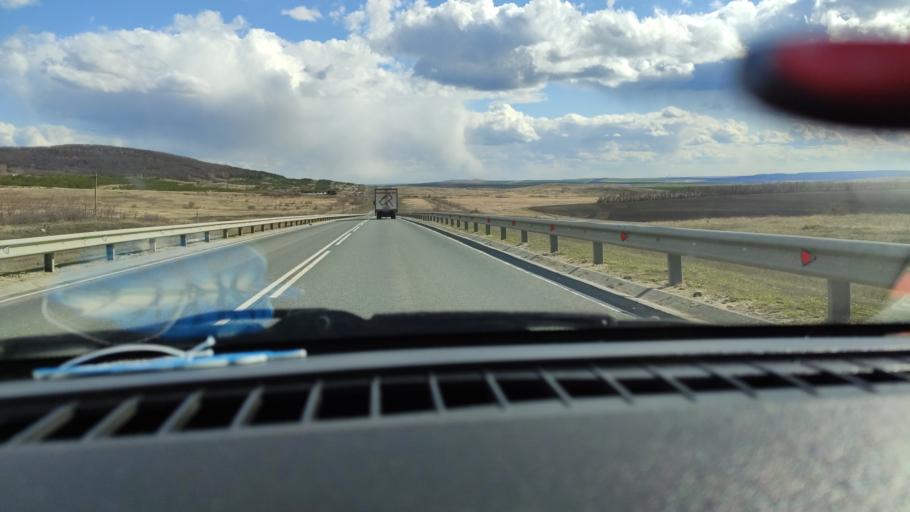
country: RU
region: Saratov
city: Alekseyevka
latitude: 52.3136
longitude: 47.9237
